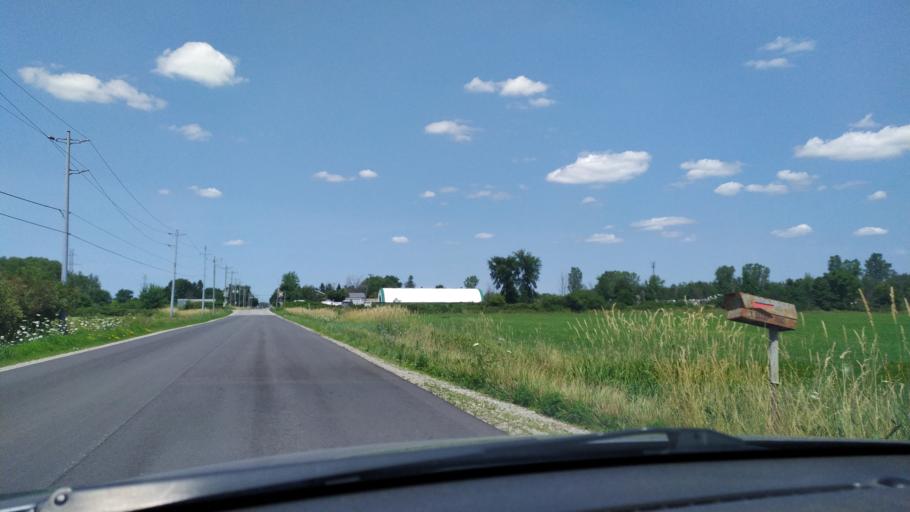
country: CA
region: Ontario
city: Stratford
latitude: 43.3649
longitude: -80.9378
